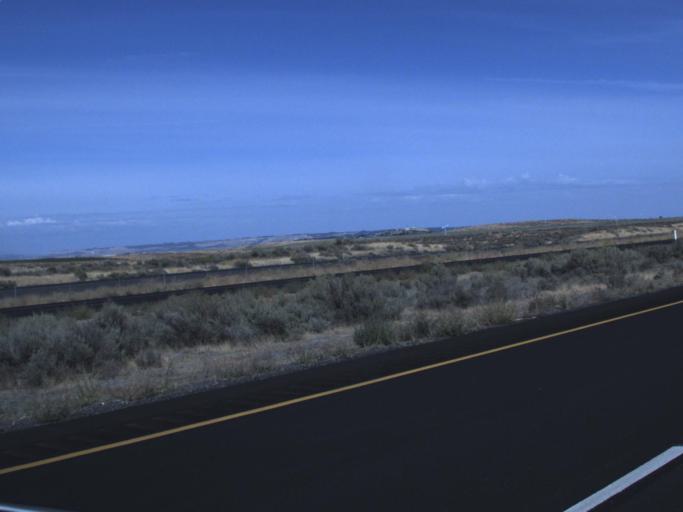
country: US
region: Washington
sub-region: Benton County
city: West Richland
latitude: 46.2607
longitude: -119.4155
